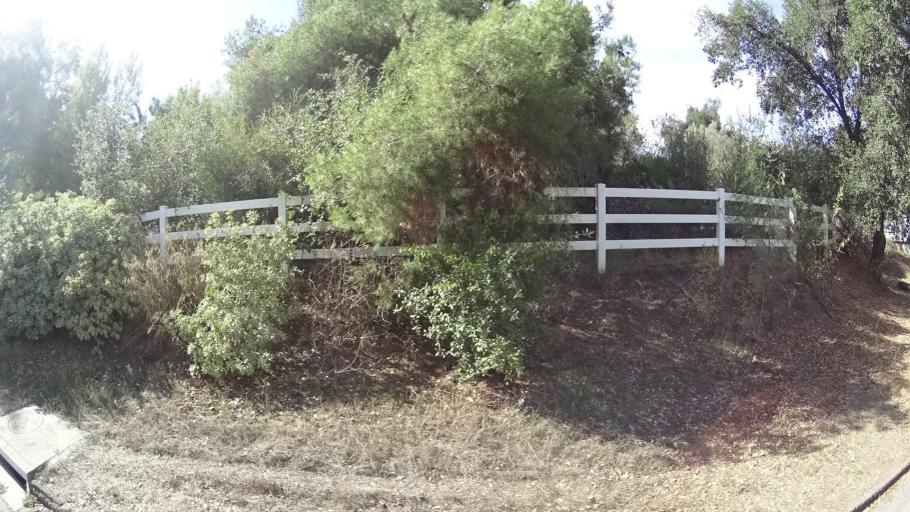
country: US
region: California
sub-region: San Diego County
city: Alpine
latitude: 32.8264
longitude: -116.7873
